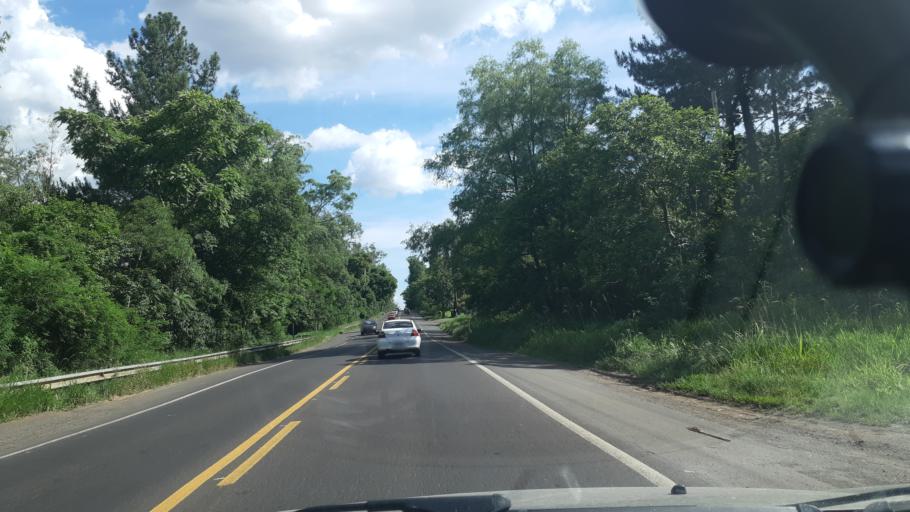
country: BR
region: Rio Grande do Sul
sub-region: Estancia Velha
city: Estancia Velha
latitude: -29.6390
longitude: -51.1421
